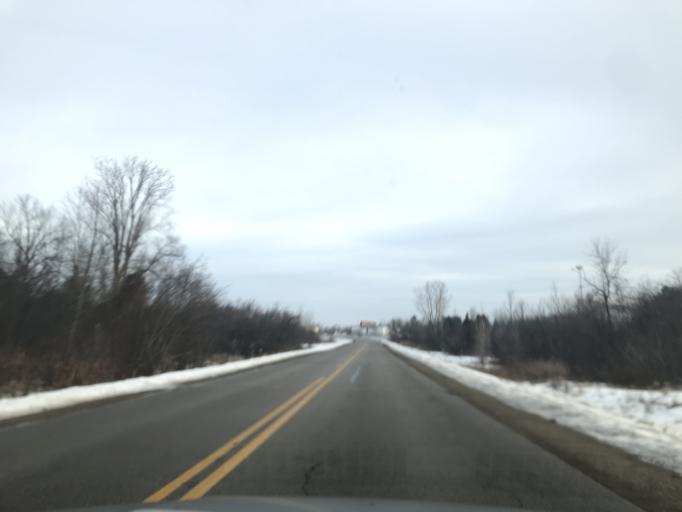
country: US
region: Wisconsin
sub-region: Brown County
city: Suamico
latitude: 44.6810
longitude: -88.0525
